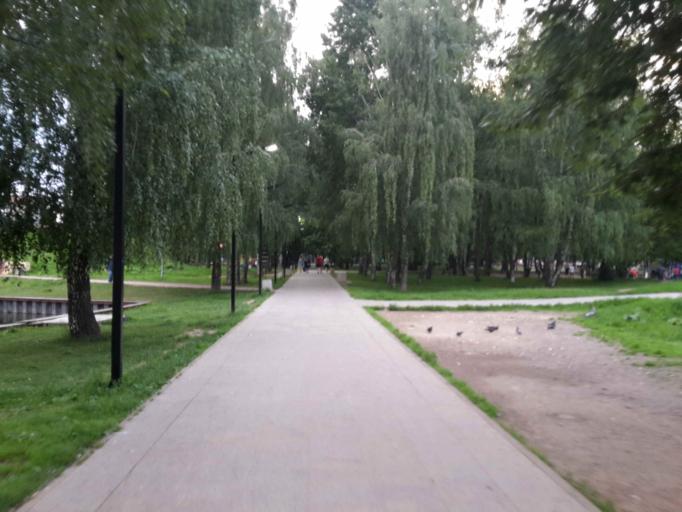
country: RU
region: Moskovskaya
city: Dolgoprudnyy
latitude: 55.9431
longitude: 37.5031
